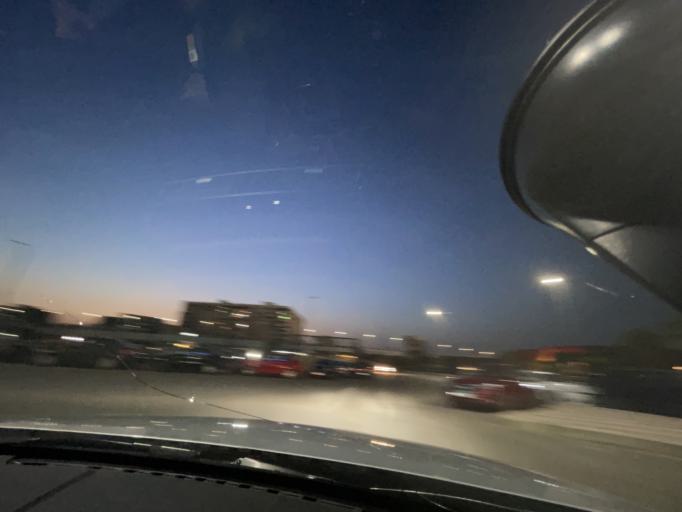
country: EG
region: Muhafazat al Qahirah
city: Cairo
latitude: 30.0699
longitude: 31.3552
